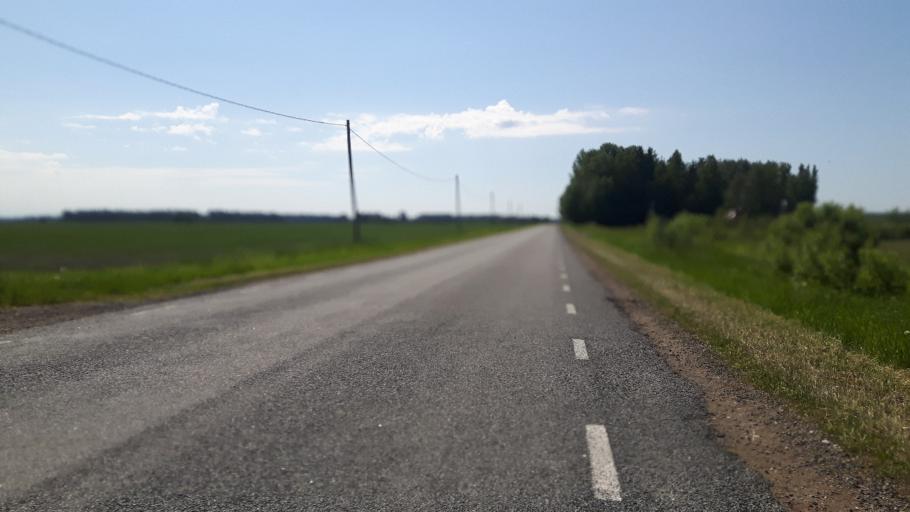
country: EE
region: Paernumaa
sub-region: Vaendra vald (alev)
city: Vandra
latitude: 58.6225
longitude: 25.0210
